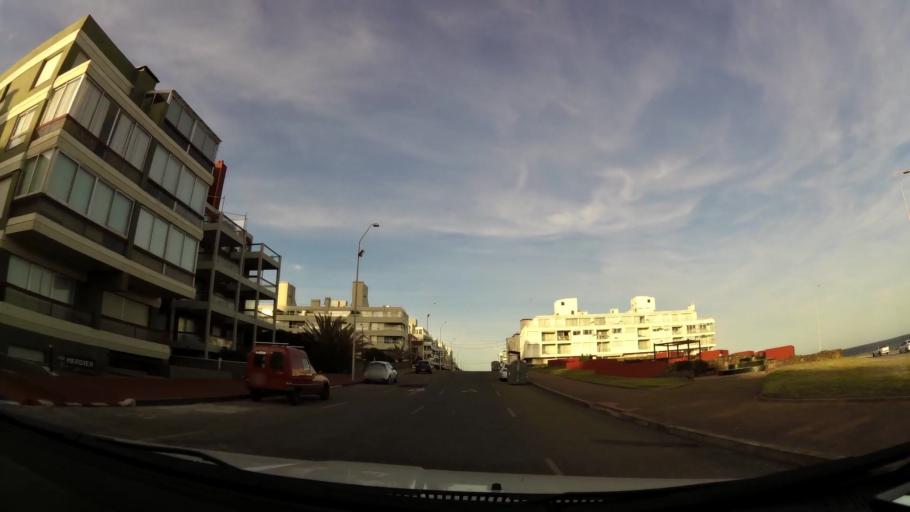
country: UY
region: Maldonado
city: Punta del Este
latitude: -34.9666
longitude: -54.9452
